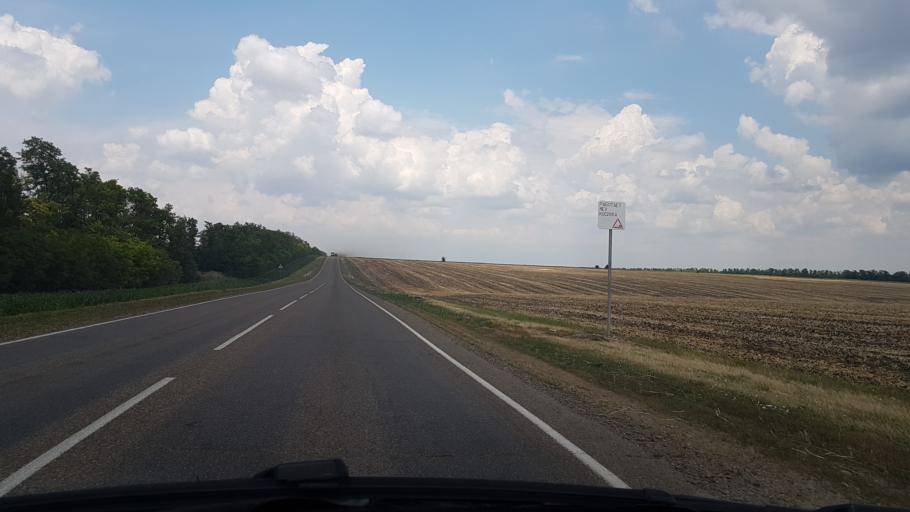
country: RU
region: Krasnodarskiy
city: Dmitriyevskaya
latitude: 45.6737
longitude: 40.7441
